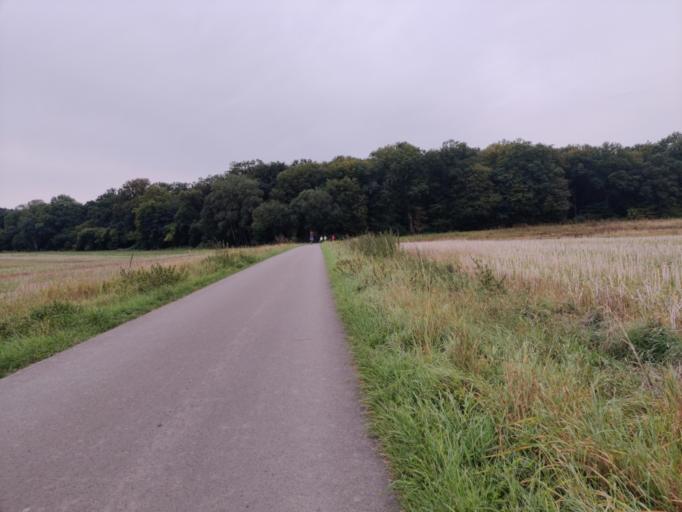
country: DE
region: Lower Saxony
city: Brevorde
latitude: 51.9072
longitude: 9.4274
